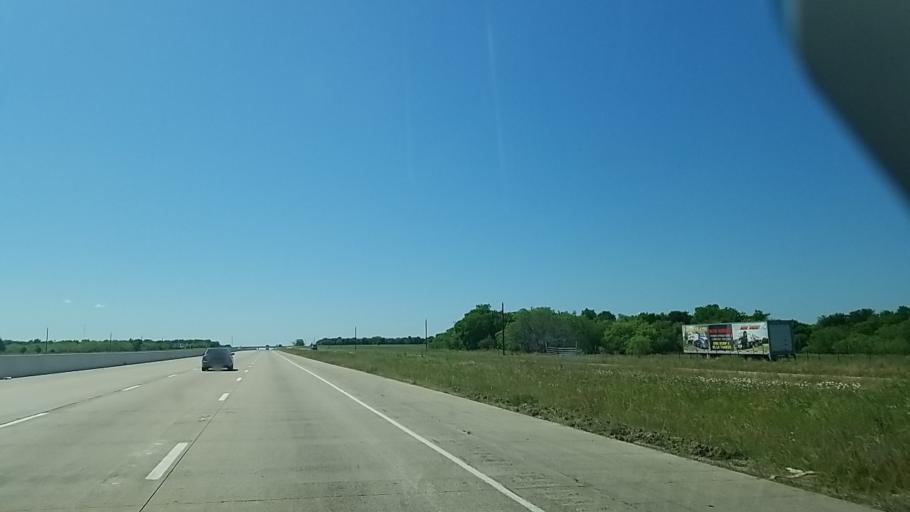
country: US
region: Texas
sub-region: Freestone County
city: Wortham
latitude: 31.8992
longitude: -96.3728
